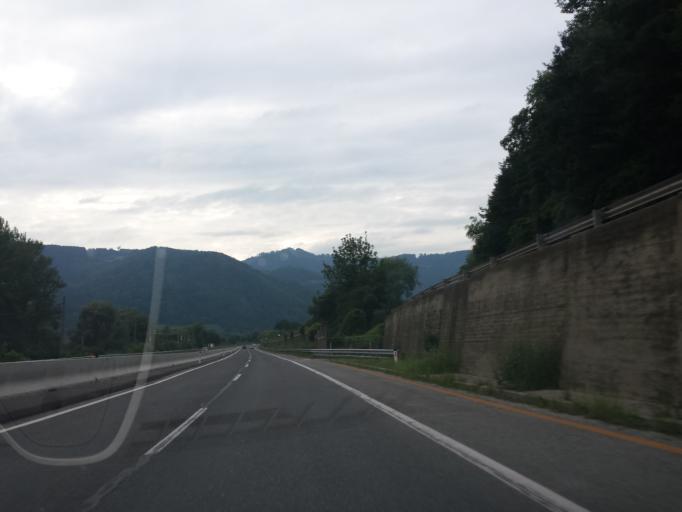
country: AT
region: Styria
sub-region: Politischer Bezirk Graz-Umgebung
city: Frohnleiten
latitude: 47.2361
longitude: 15.3310
